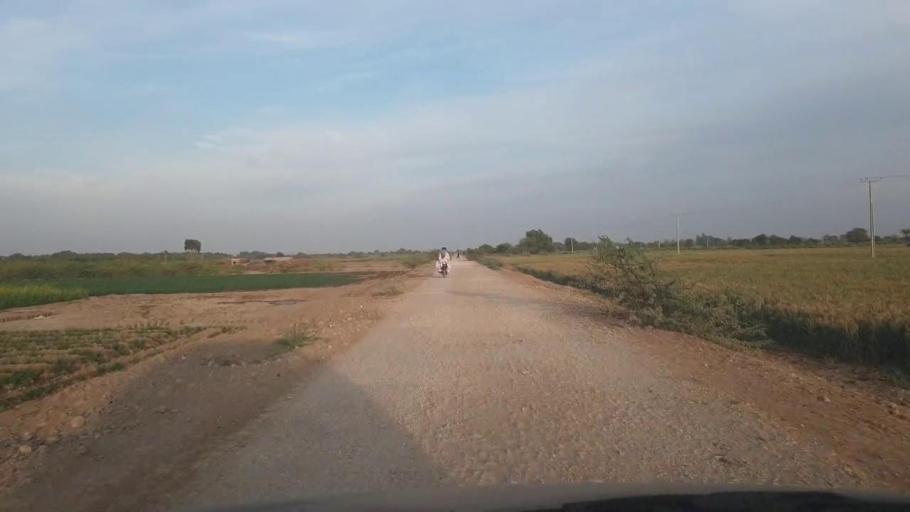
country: PK
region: Sindh
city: Kunri
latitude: 25.2269
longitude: 69.5620
